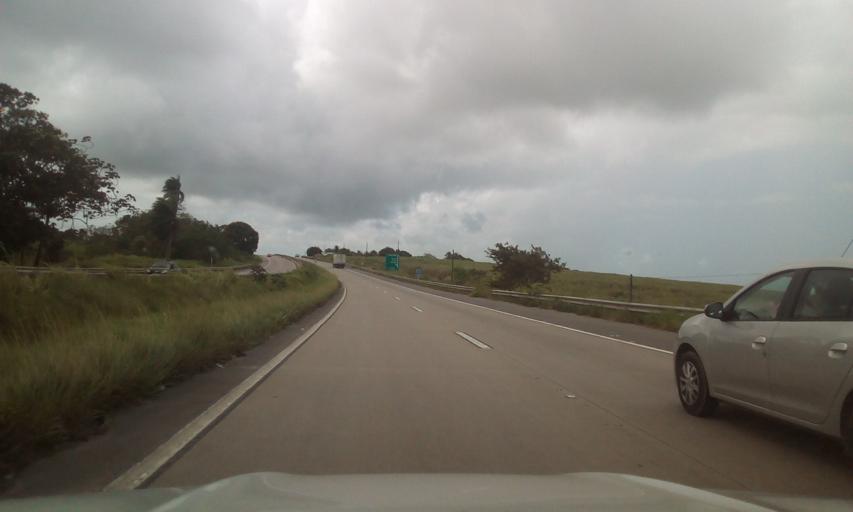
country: BR
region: Pernambuco
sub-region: Itapissuma
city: Itapissuma
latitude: -7.7086
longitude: -34.9283
